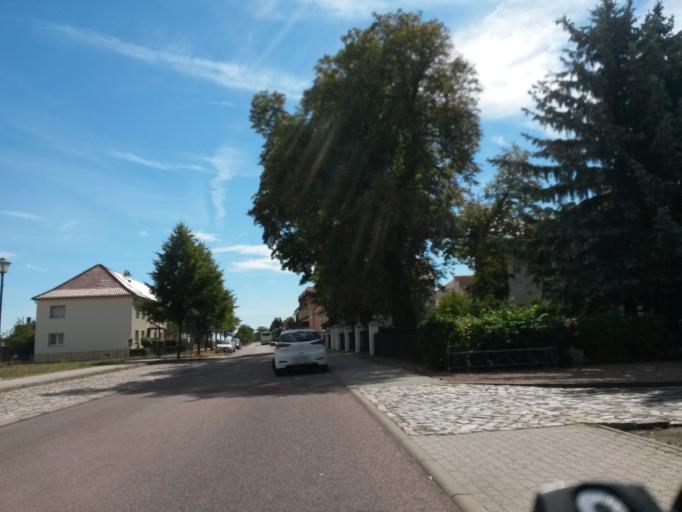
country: DE
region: Saxony-Anhalt
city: Worlitz
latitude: 51.8393
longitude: 12.4278
